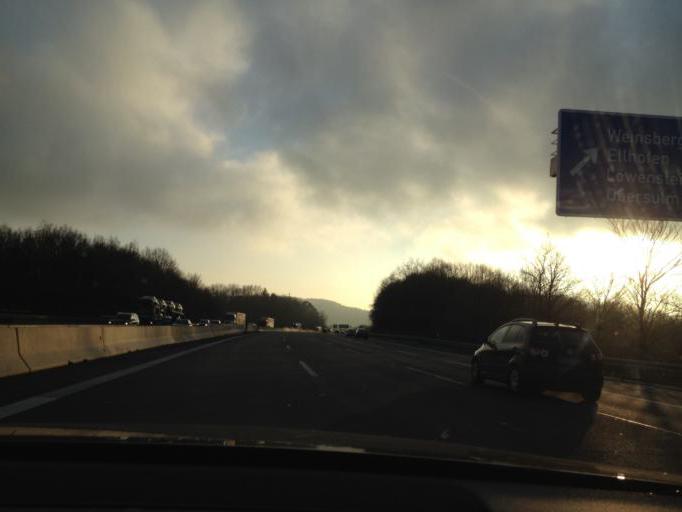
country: DE
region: Baden-Wuerttemberg
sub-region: Regierungsbezirk Stuttgart
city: Ellhofen
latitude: 49.1380
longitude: 9.3058
